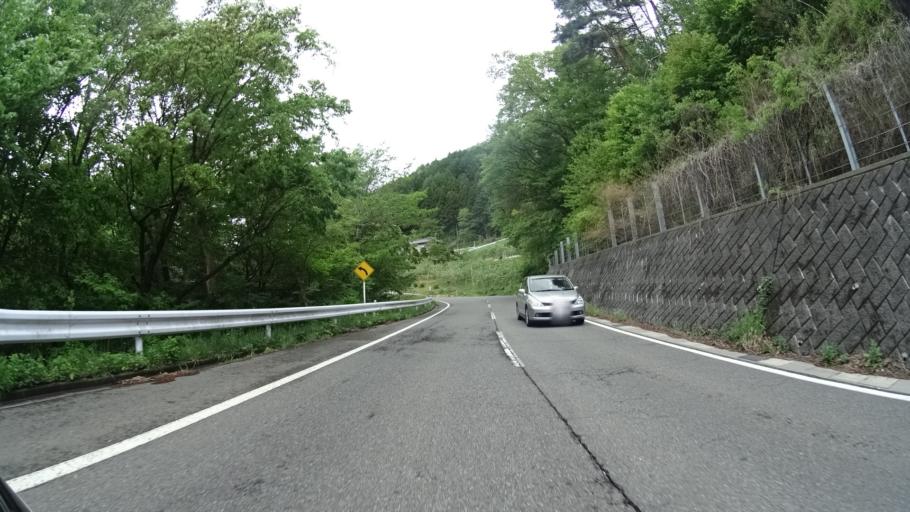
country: JP
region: Nagano
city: Nagano-shi
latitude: 36.6938
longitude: 138.2052
